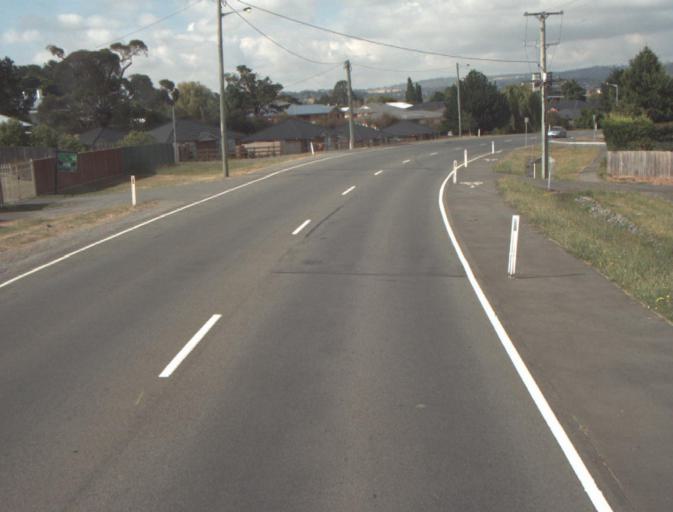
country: AU
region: Tasmania
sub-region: Launceston
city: Newstead
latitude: -41.4567
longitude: 147.1979
